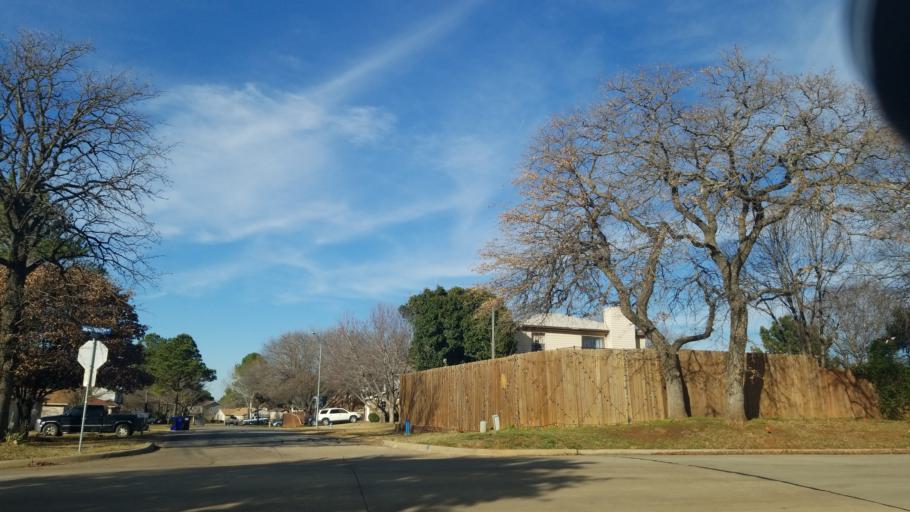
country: US
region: Texas
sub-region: Denton County
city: Corinth
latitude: 33.1358
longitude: -97.0632
